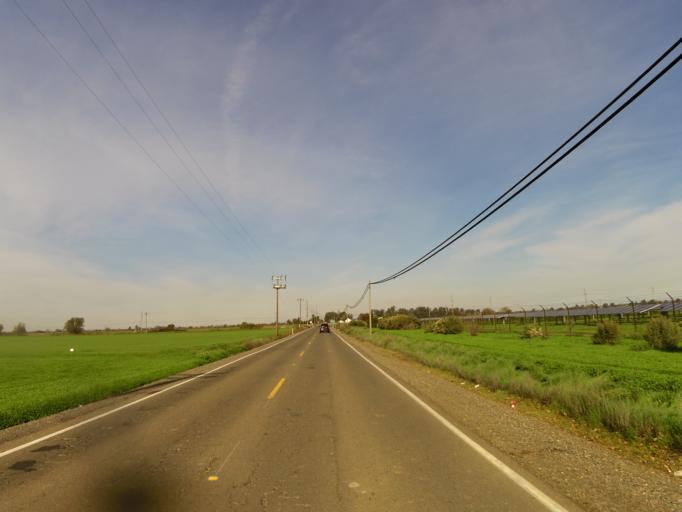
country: US
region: California
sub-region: Sacramento County
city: Laguna
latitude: 38.3479
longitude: -121.4174
